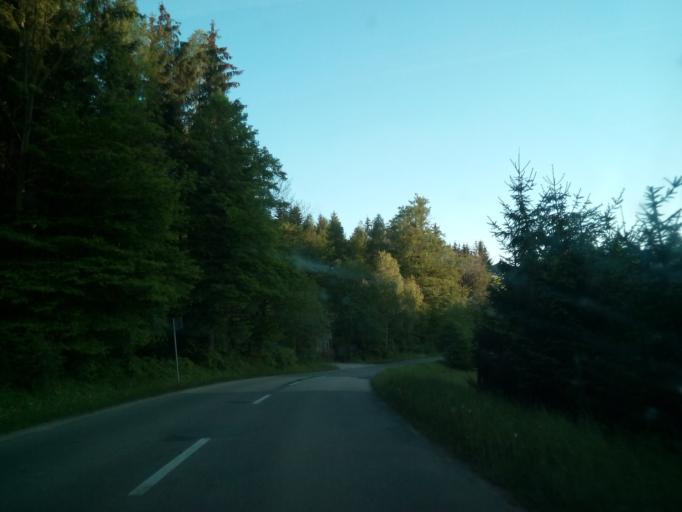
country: CZ
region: South Moravian
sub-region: Okres Blansko
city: Jedovnice
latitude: 49.3074
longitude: 16.7464
